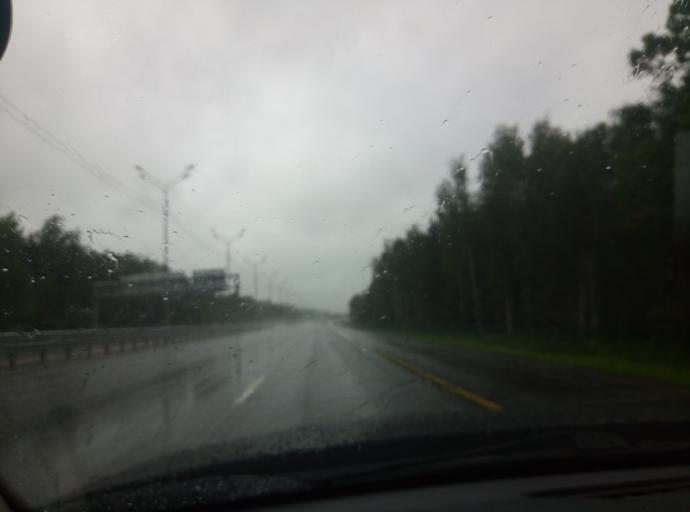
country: RU
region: Moskovskaya
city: Danki
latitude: 54.9864
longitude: 37.5362
